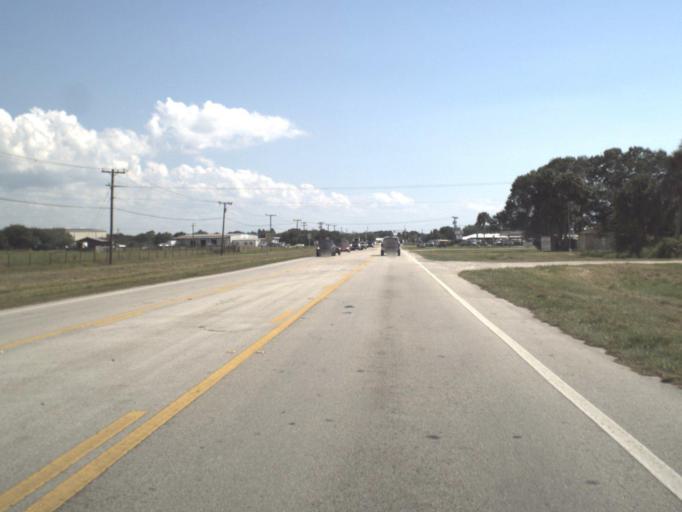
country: US
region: Florida
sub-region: Okeechobee County
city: Okeechobee
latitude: 27.2549
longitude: -80.8553
